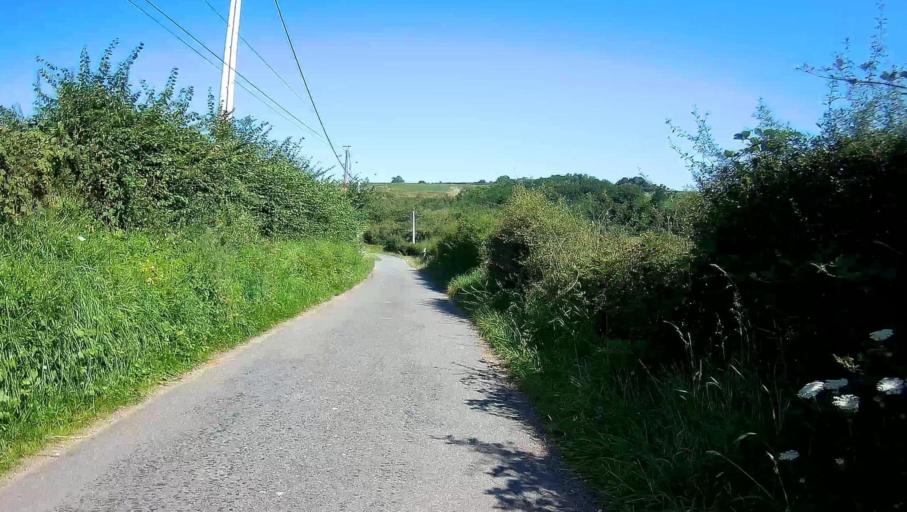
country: FR
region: Bourgogne
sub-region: Departement de Saone-et-Loire
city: Couches
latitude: 46.8450
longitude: 4.5737
